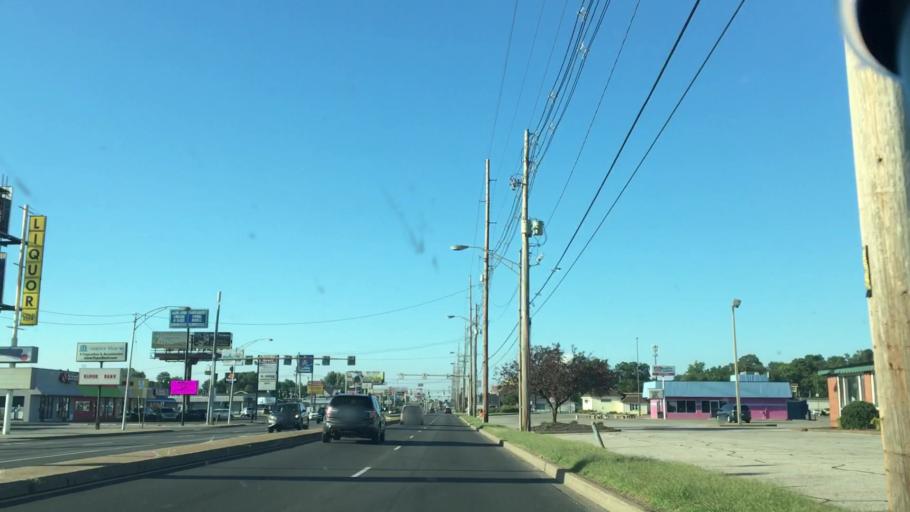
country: US
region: Indiana
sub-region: Vanderburgh County
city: Evansville
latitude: 37.9642
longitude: -87.4926
